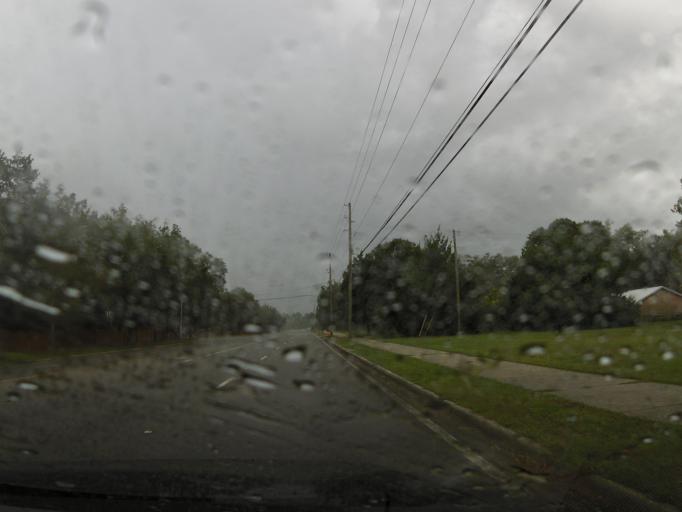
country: US
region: Florida
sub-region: Clay County
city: Asbury Lake
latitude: 30.0355
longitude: -81.8097
